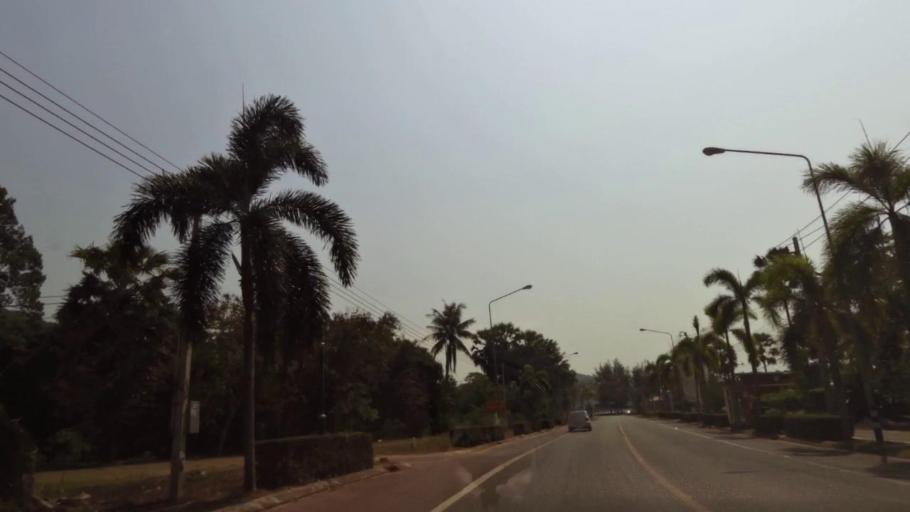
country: TH
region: Chanthaburi
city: Tha Mai
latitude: 12.5346
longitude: 101.9417
